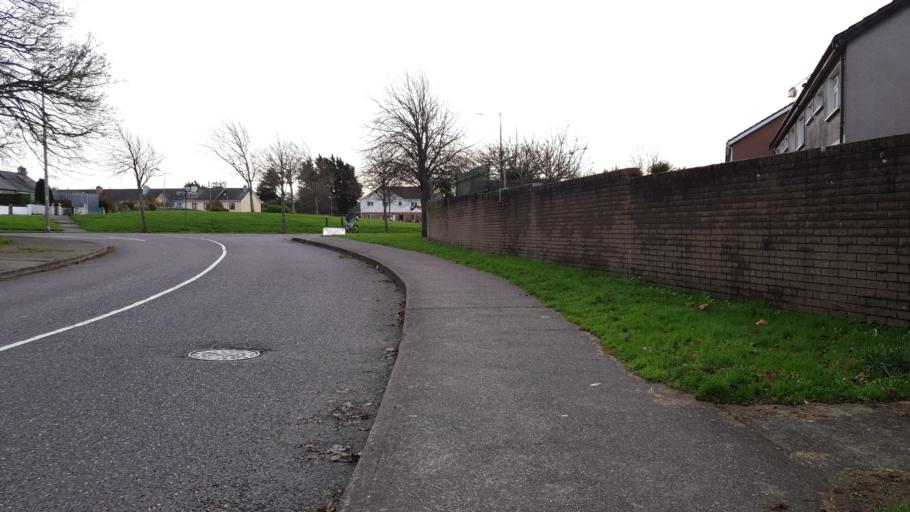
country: IE
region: Munster
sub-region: County Cork
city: Cork
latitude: 51.8938
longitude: -8.4084
